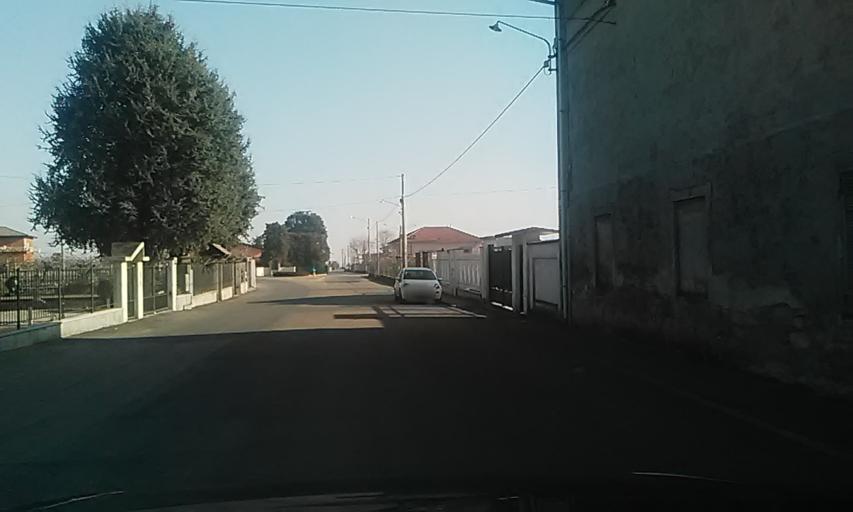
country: IT
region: Piedmont
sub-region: Provincia di Vercelli
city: Borgo d'Ale
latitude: 45.3503
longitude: 8.0565
